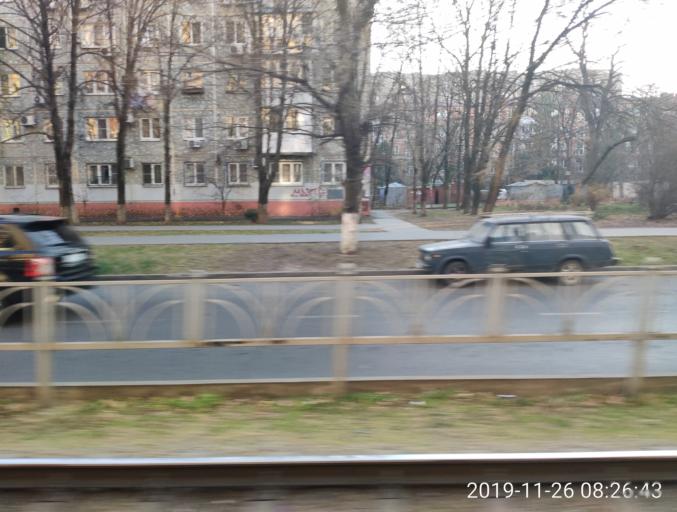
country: RU
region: Krasnodarskiy
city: Krasnodar
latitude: 45.0611
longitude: 39.0020
